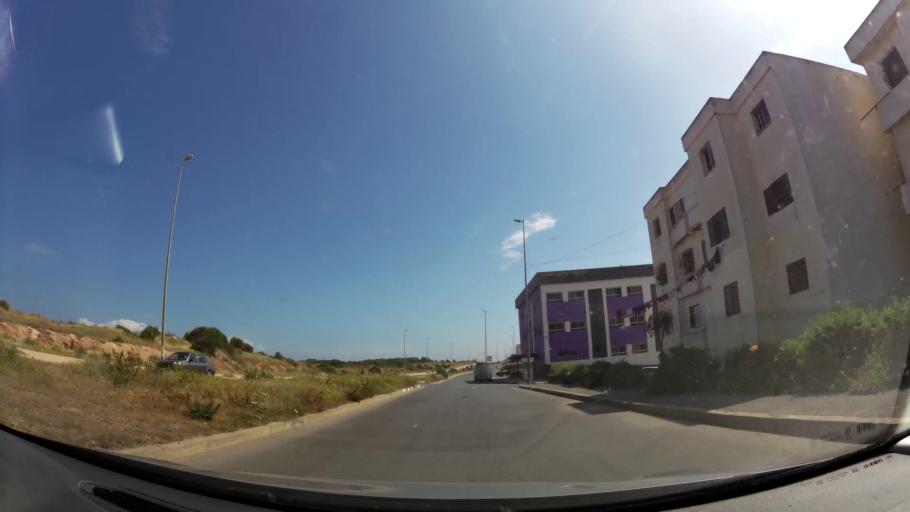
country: MA
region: Rabat-Sale-Zemmour-Zaer
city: Sale
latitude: 34.0775
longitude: -6.7950
